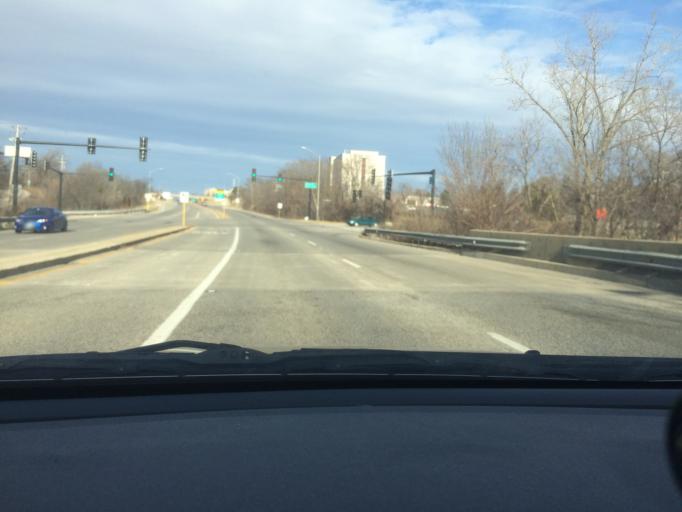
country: US
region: Illinois
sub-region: Kane County
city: Elgin
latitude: 42.0616
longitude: -88.2927
